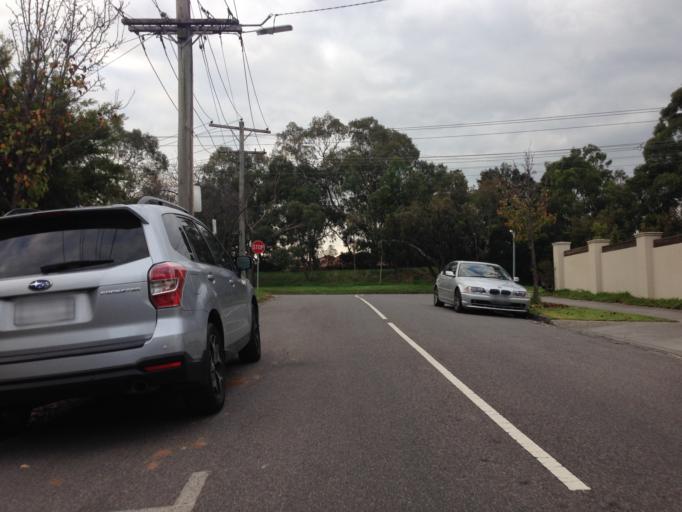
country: AU
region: Victoria
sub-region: Boroondara
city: Kew East
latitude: -37.7983
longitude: 145.0448
